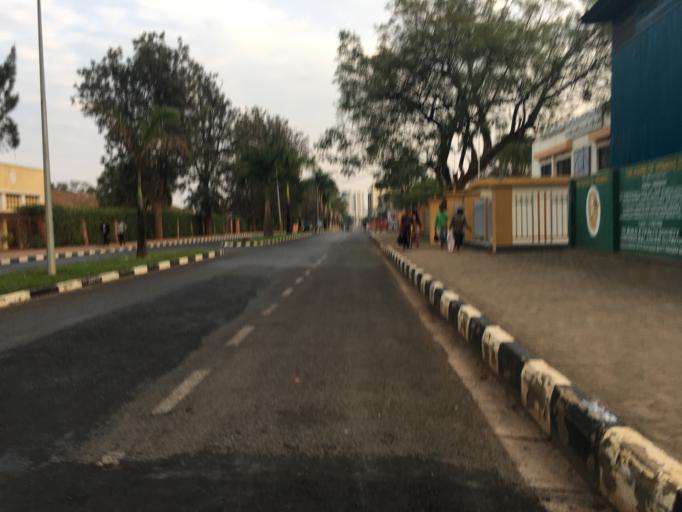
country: RW
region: Kigali
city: Kigali
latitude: -1.9542
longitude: 30.0608
